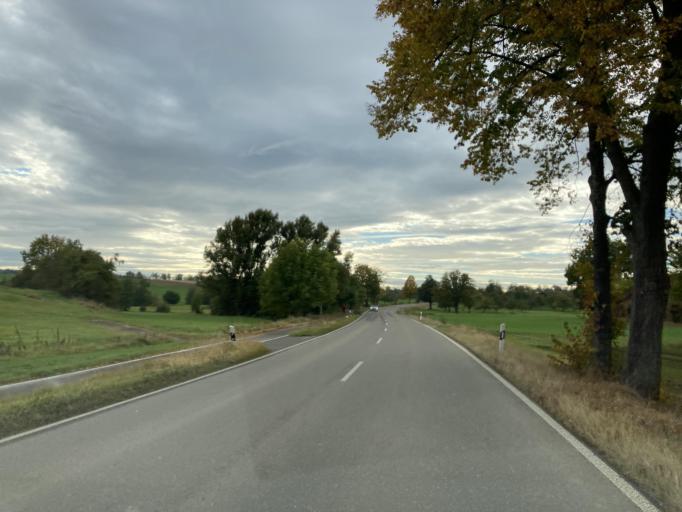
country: DE
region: Baden-Wuerttemberg
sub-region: Regierungsbezirk Stuttgart
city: Bondorf
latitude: 48.5047
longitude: 8.8706
